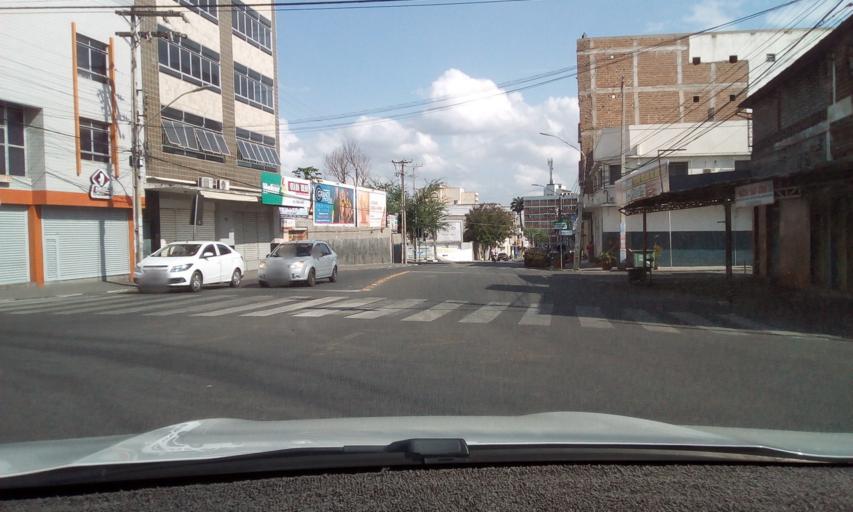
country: BR
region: Pernambuco
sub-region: Caruaru
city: Caruaru
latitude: -8.2802
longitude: -35.9730
